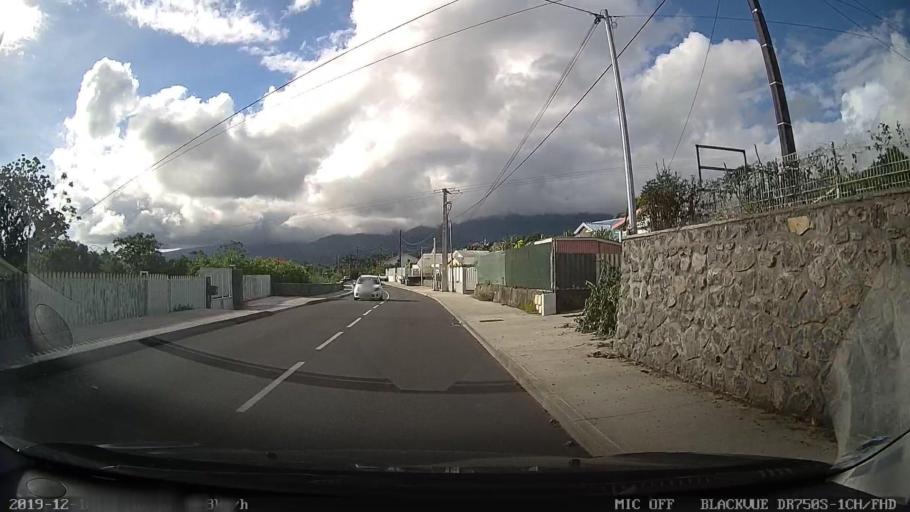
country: RE
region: Reunion
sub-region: Reunion
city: Le Tampon
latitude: -21.2475
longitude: 55.5183
